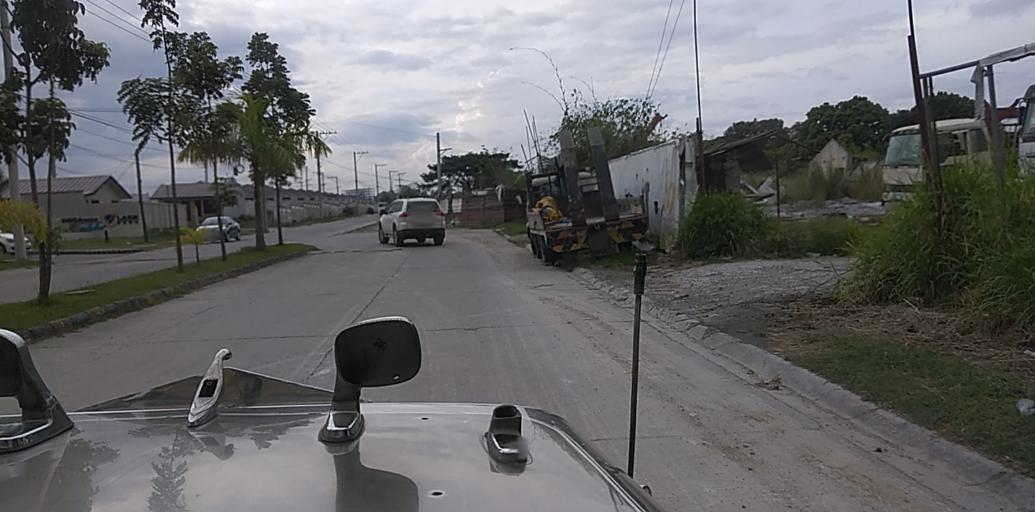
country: PH
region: Central Luzon
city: Santol
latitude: 15.1663
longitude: 120.5390
